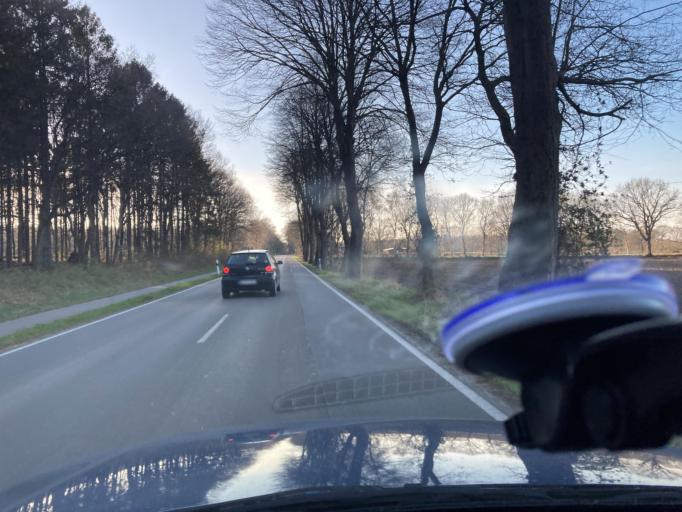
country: DE
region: Schleswig-Holstein
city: Weddingstedt
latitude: 54.2263
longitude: 9.1113
